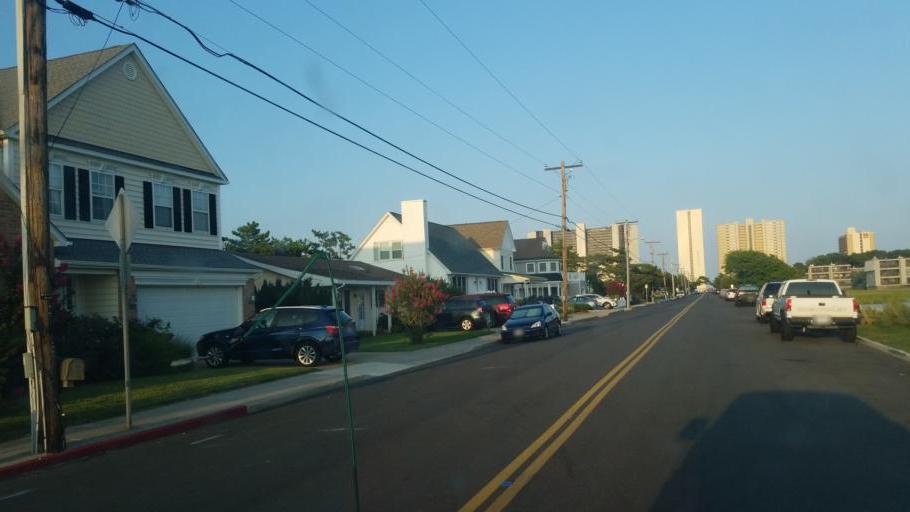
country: US
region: Maryland
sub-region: Worcester County
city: Ocean City
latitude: 38.4163
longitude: -75.0643
